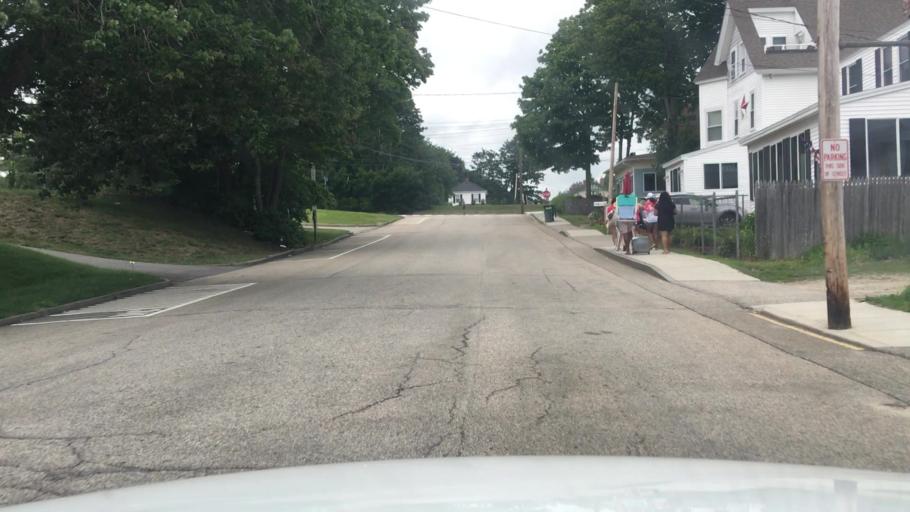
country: US
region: Maine
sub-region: York County
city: Old Orchard Beach
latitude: 43.5163
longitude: -70.3770
